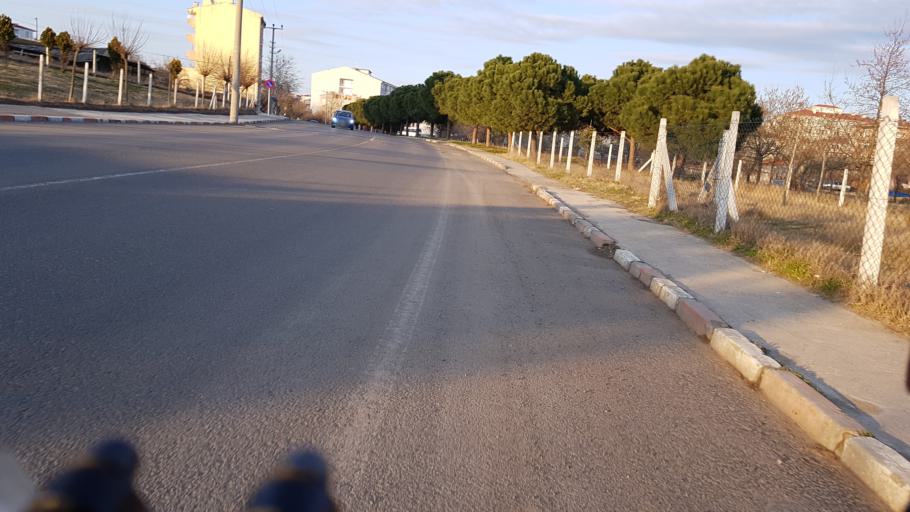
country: TR
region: Tekirdag
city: Velimese
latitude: 41.2503
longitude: 27.8744
